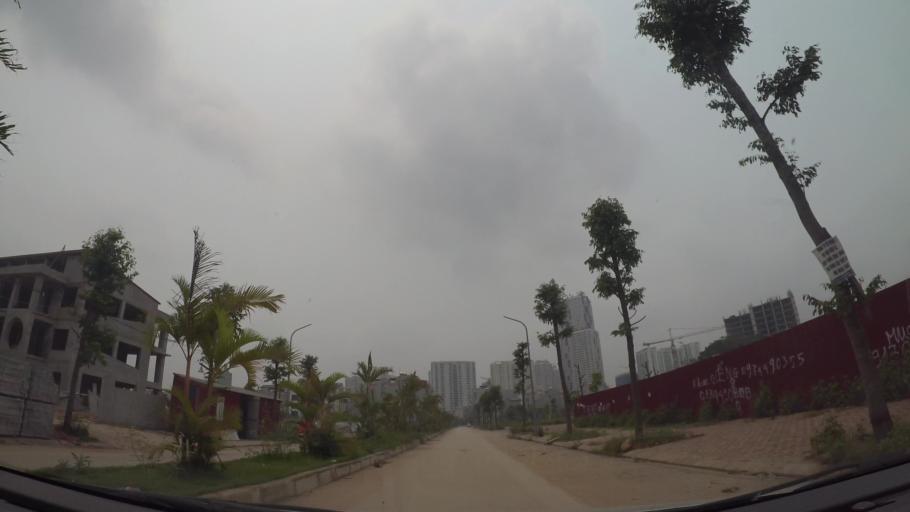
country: VN
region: Ha Noi
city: Ha Dong
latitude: 20.9781
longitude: 105.7680
